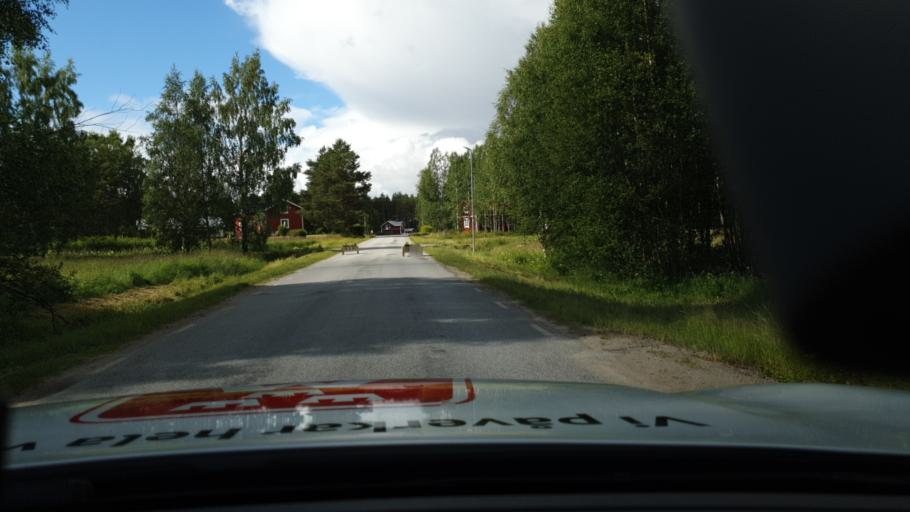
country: SE
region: Norrbotten
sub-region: Pitea Kommun
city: Rosvik
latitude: 65.3911
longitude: 21.7337
